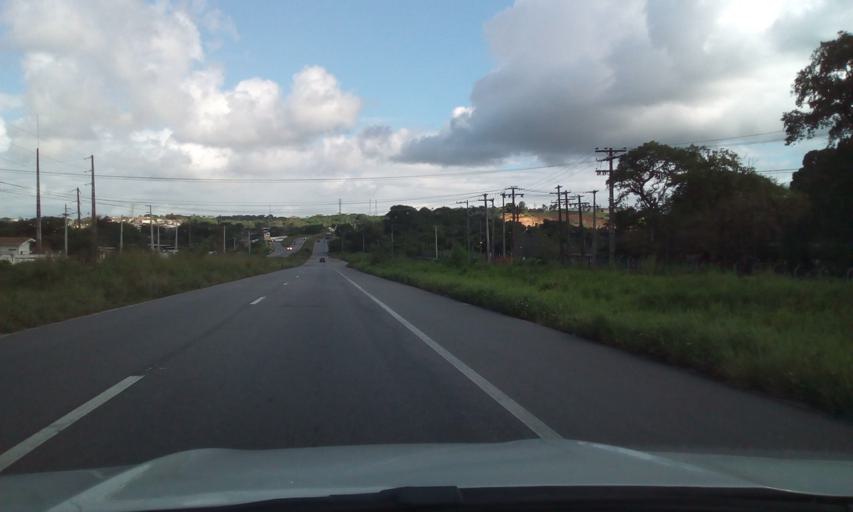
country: BR
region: Pernambuco
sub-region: Abreu E Lima
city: Abreu e Lima
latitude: -7.9408
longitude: -34.9039
